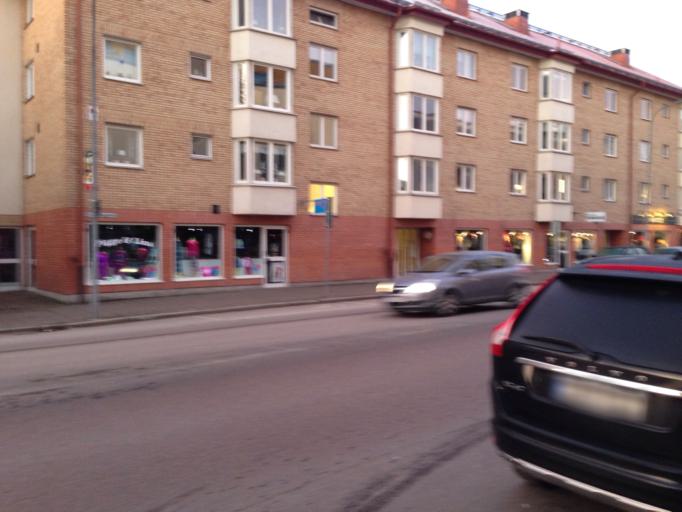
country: SE
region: Vaermland
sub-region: Karlstads Kommun
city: Karlstad
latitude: 59.3792
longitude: 13.5059
